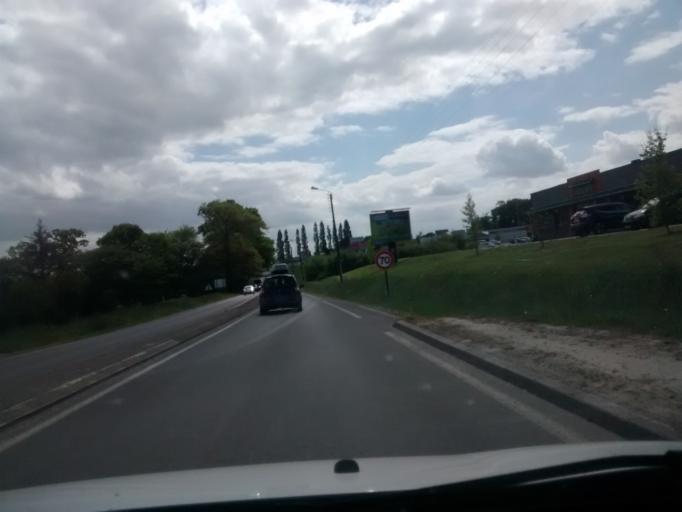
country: FR
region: Brittany
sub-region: Departement des Cotes-d'Armor
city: Saint-Samson-sur-Rance
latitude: 48.4747
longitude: -2.0430
